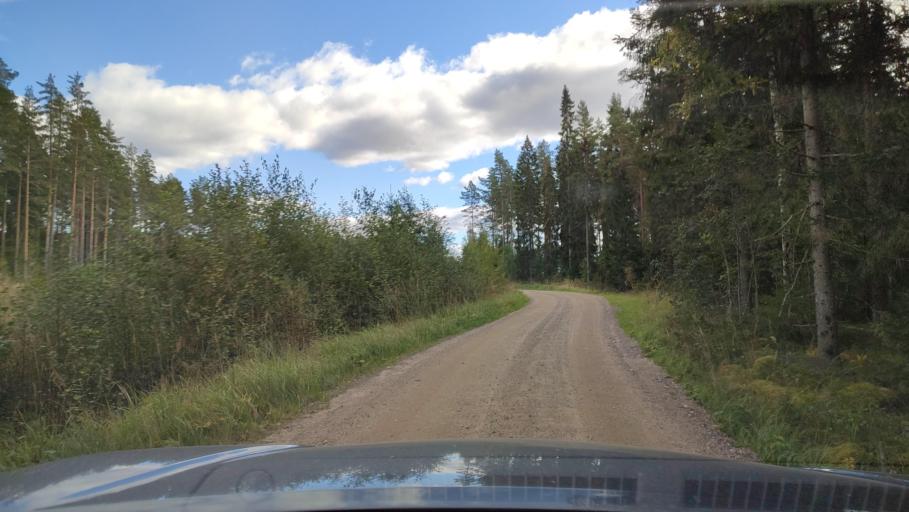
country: FI
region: Southern Ostrobothnia
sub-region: Suupohja
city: Karijoki
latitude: 62.2034
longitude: 21.6045
